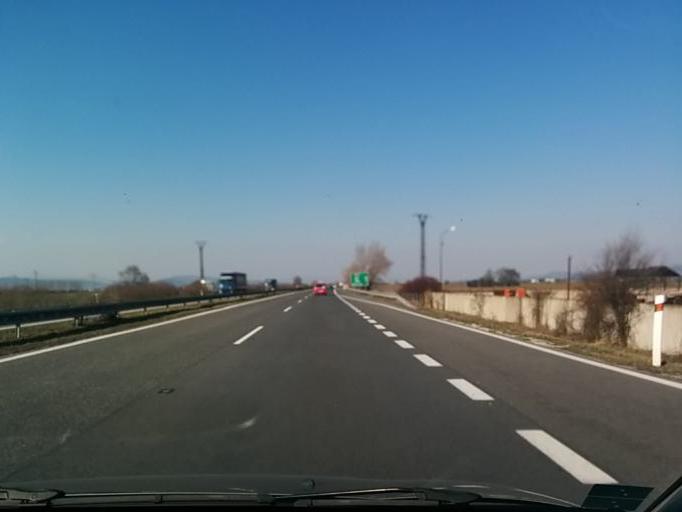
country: SK
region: Trnavsky
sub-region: Okres Trnava
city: Piestany
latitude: 48.5941
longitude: 17.7909
